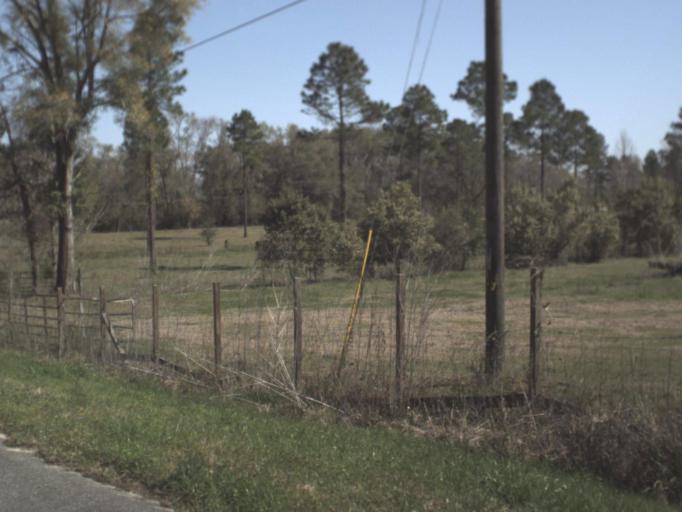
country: US
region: Florida
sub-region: Jefferson County
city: Monticello
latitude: 30.5156
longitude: -84.0243
